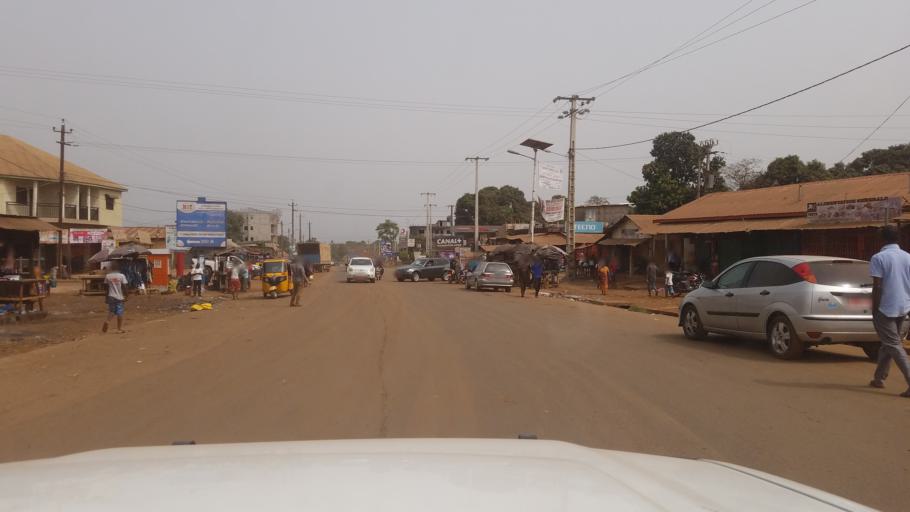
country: GN
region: Kindia
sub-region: Prefecture de Dubreka
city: Dubreka
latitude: 9.6707
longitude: -13.5840
